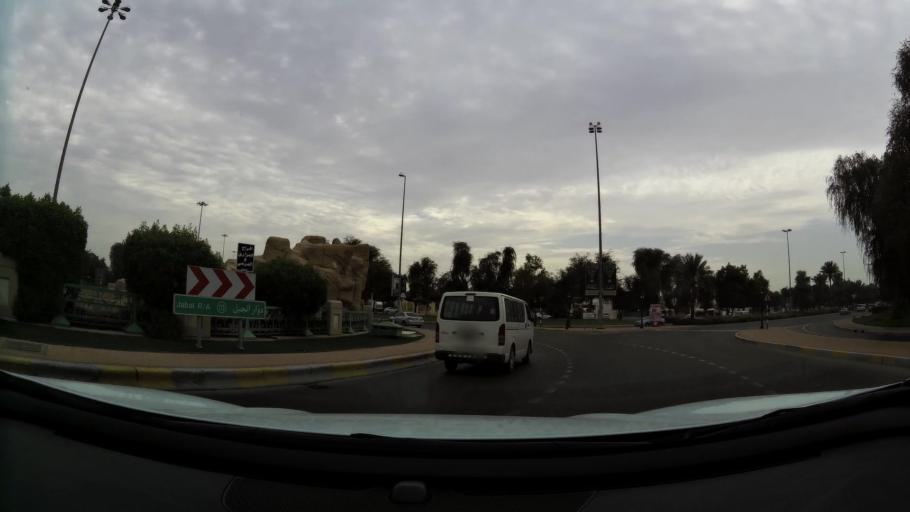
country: AE
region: Abu Dhabi
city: Al Ain
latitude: 24.2245
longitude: 55.7377
